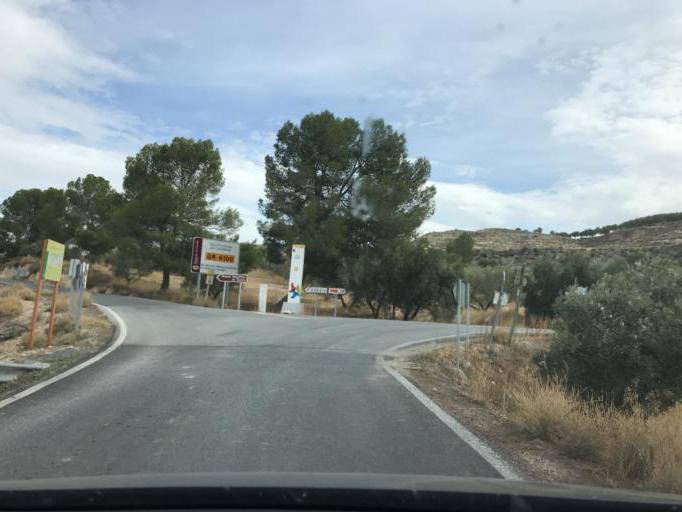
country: ES
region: Andalusia
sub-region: Provincia de Granada
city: Villanueva de las Torres
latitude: 37.5094
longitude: -3.1055
